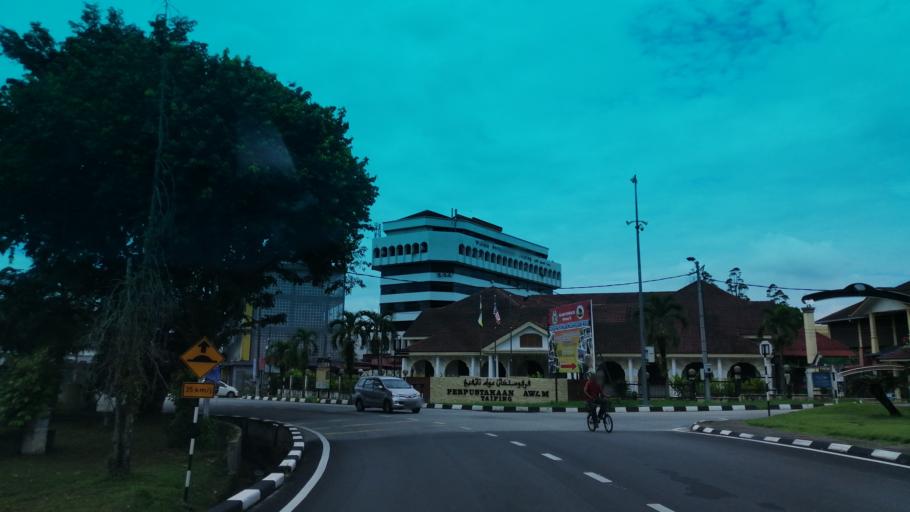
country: MY
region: Perak
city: Taiping
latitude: 4.8542
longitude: 100.7452
